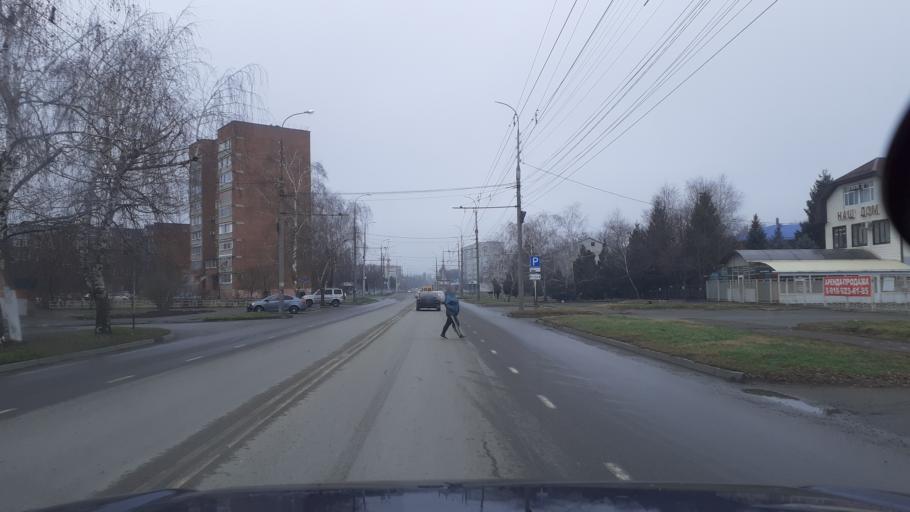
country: RU
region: Adygeya
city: Maykop
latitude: 44.6236
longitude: 40.0700
